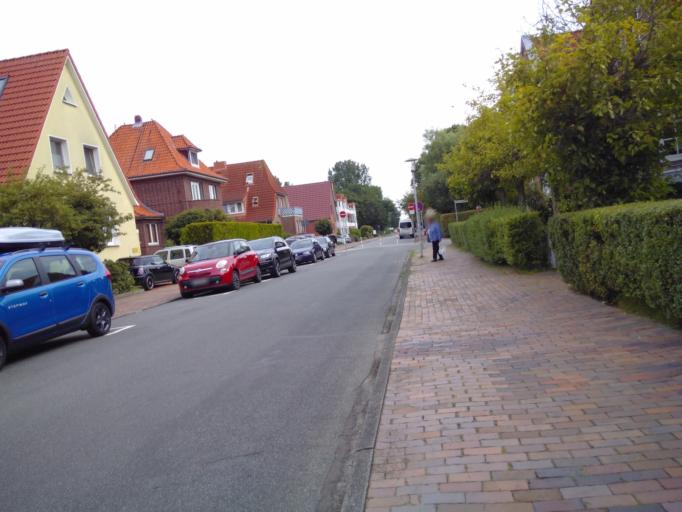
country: DE
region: Lower Saxony
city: Cuxhaven
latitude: 53.8876
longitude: 8.6770
